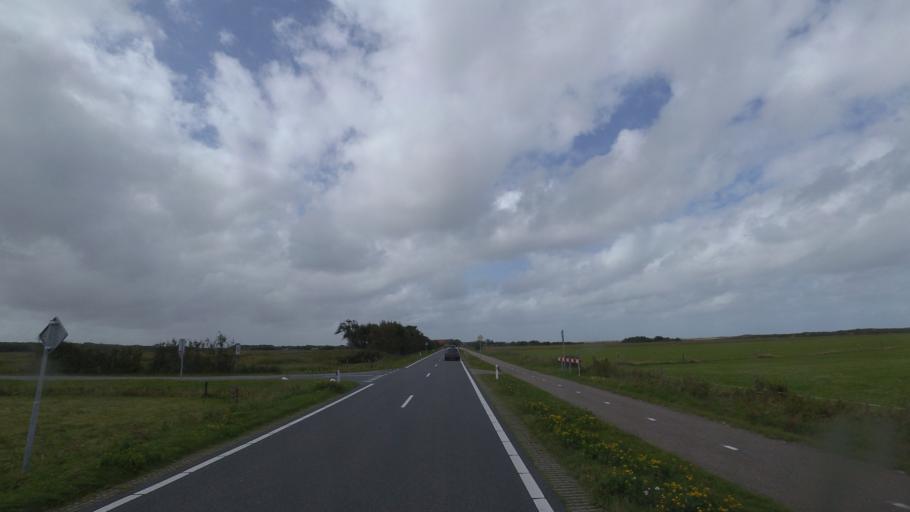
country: NL
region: Friesland
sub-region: Gemeente Ameland
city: Hollum
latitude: 53.4465
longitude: 5.6760
